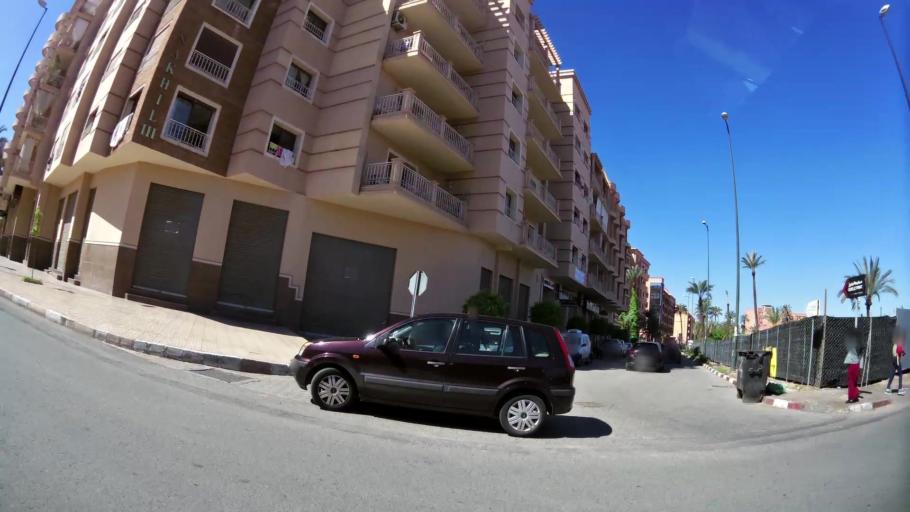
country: MA
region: Marrakech-Tensift-Al Haouz
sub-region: Marrakech
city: Marrakesh
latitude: 31.6395
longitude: -8.0095
